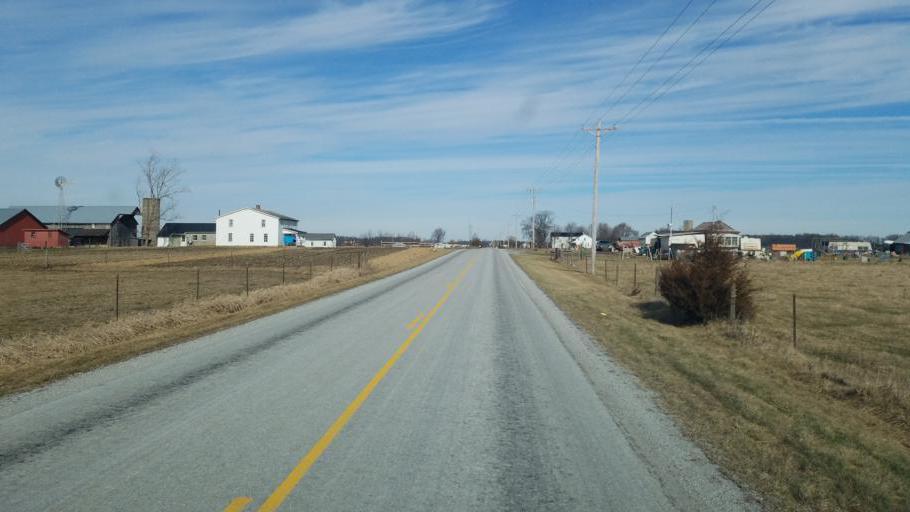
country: US
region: Ohio
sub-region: Hardin County
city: Kenton
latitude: 40.5961
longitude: -83.5042
